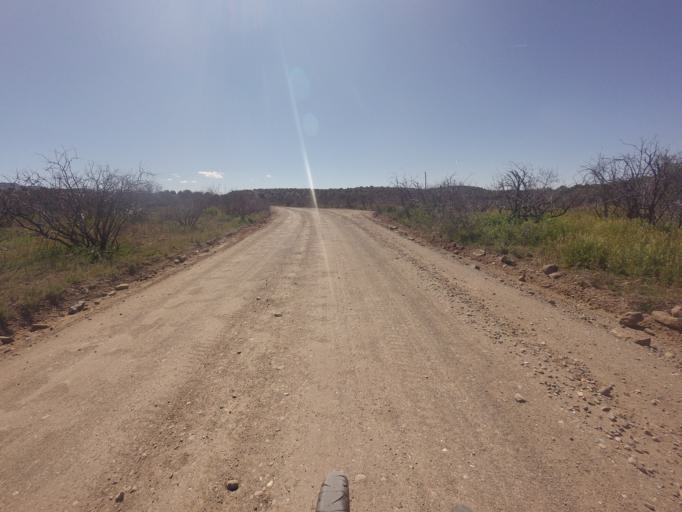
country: US
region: Arizona
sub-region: Yavapai County
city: Lake Montezuma
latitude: 34.6471
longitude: -111.7209
